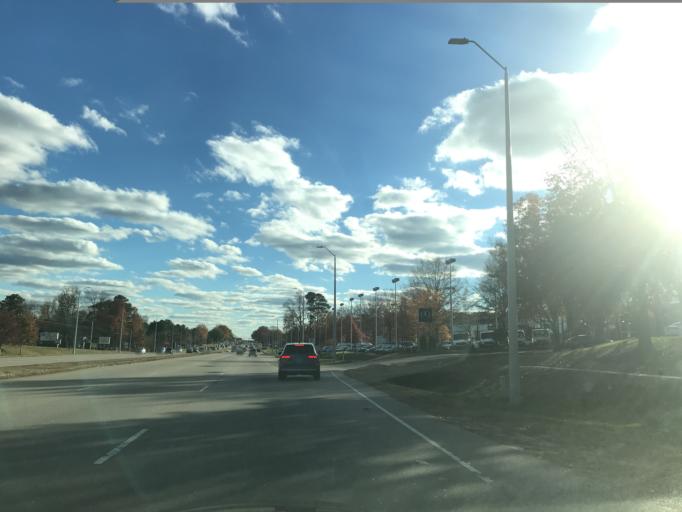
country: US
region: North Carolina
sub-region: Wake County
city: Raleigh
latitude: 35.8650
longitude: -78.5823
